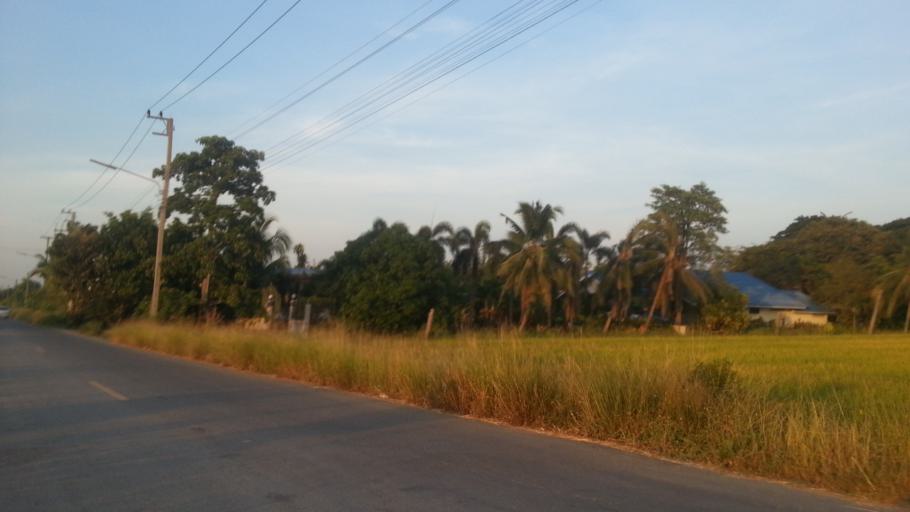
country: TH
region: Pathum Thani
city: Nong Suea
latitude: 14.0427
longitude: 100.8667
